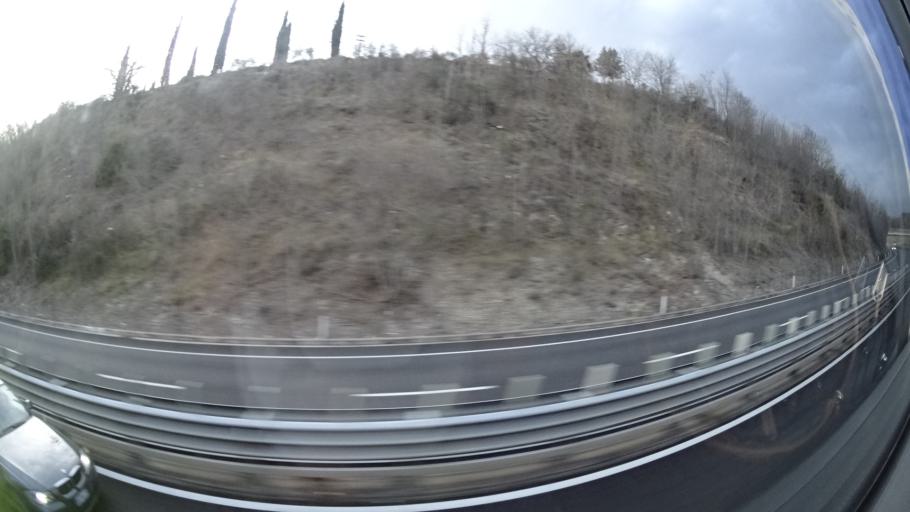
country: IT
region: Tuscany
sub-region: Province of Florence
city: Sambuca
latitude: 43.5360
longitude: 11.2203
